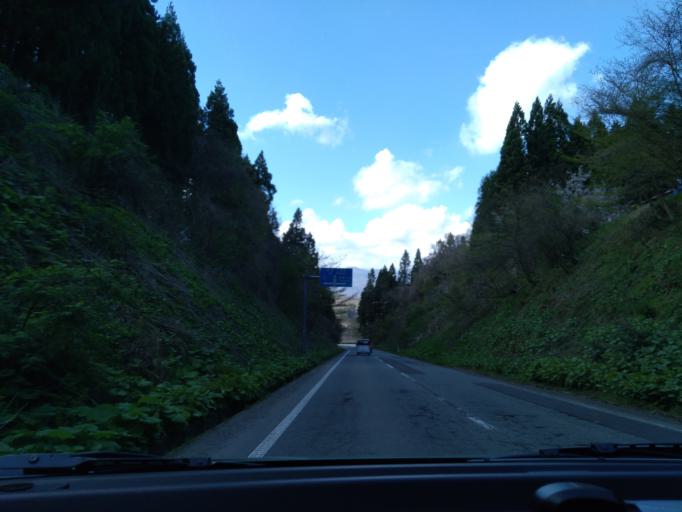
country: JP
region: Akita
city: Akita
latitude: 39.6910
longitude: 140.2747
